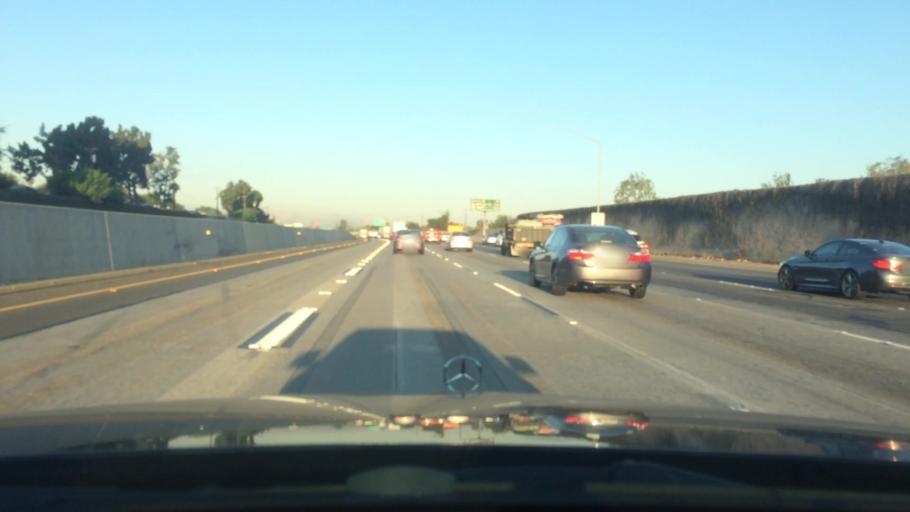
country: US
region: California
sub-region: Orange County
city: Fullerton
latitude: 33.8540
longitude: -117.9286
